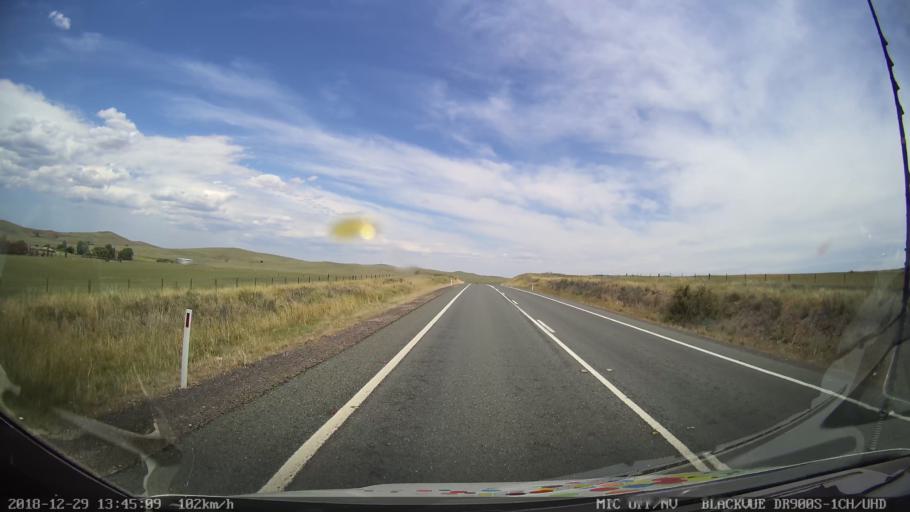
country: AU
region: New South Wales
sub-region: Cooma-Monaro
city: Cooma
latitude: -36.0922
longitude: 149.1453
